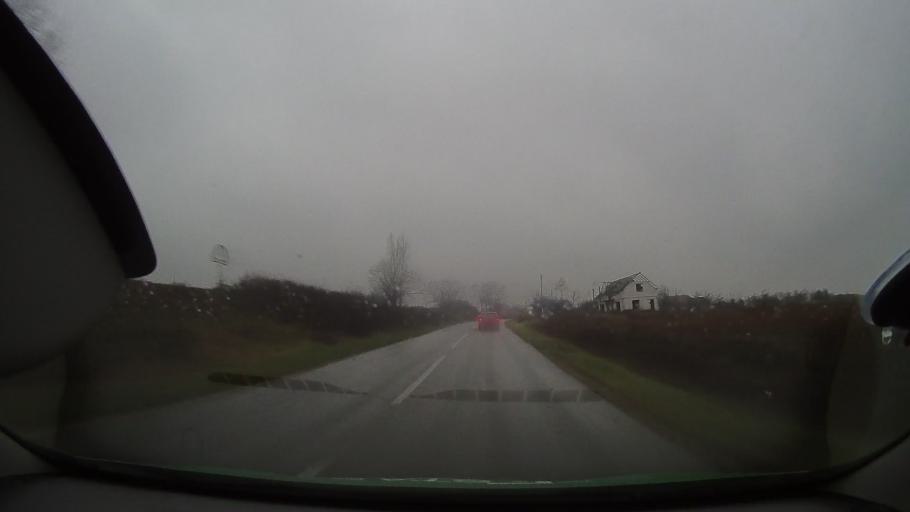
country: RO
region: Arad
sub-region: Comuna Craiova
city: Craiova
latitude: 46.5896
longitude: 21.9772
